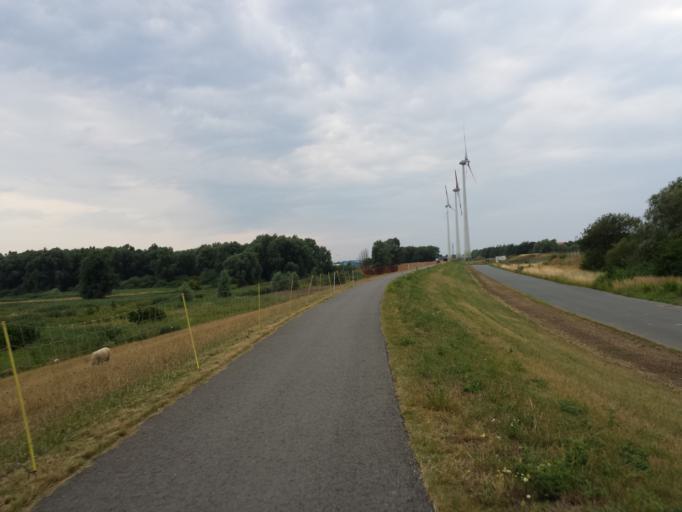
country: DE
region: Lower Saxony
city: Ritterhude
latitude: 53.1089
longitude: 8.7267
